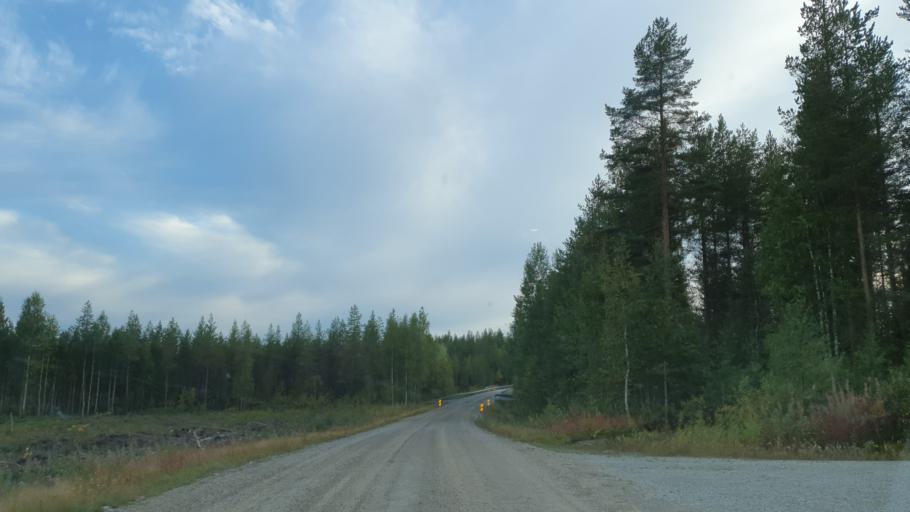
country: FI
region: Kainuu
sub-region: Kehys-Kainuu
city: Kuhmo
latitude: 64.3832
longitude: 29.5572
